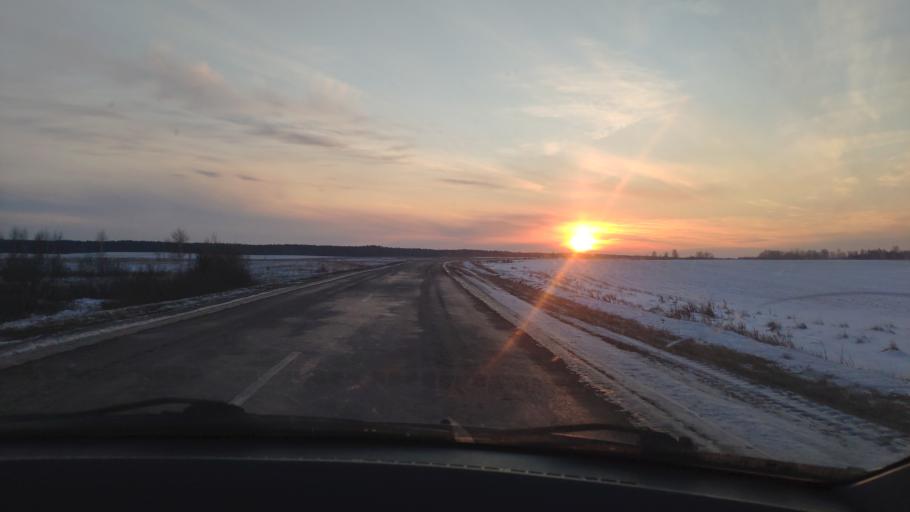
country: RU
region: Kurgan
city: Kataysk
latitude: 55.8889
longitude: 62.5355
